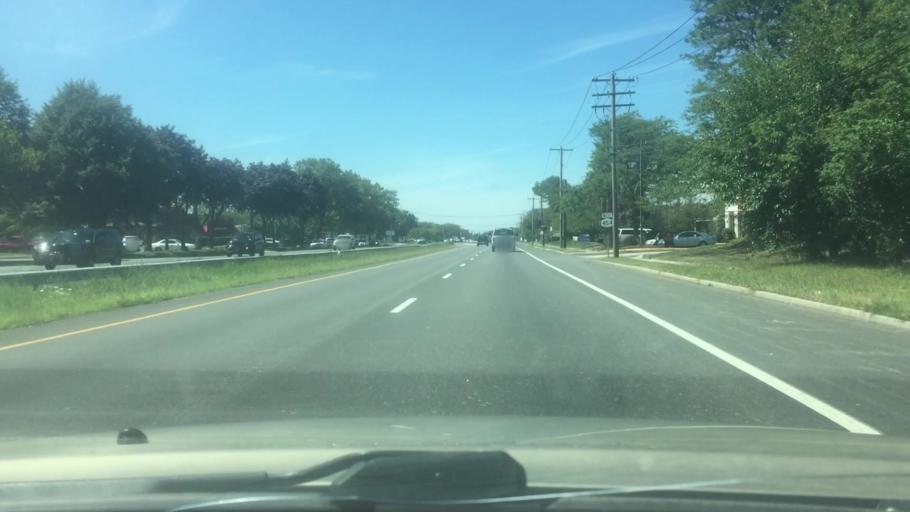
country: US
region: New York
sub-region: Suffolk County
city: Bohemia
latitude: 40.7844
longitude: -73.1082
